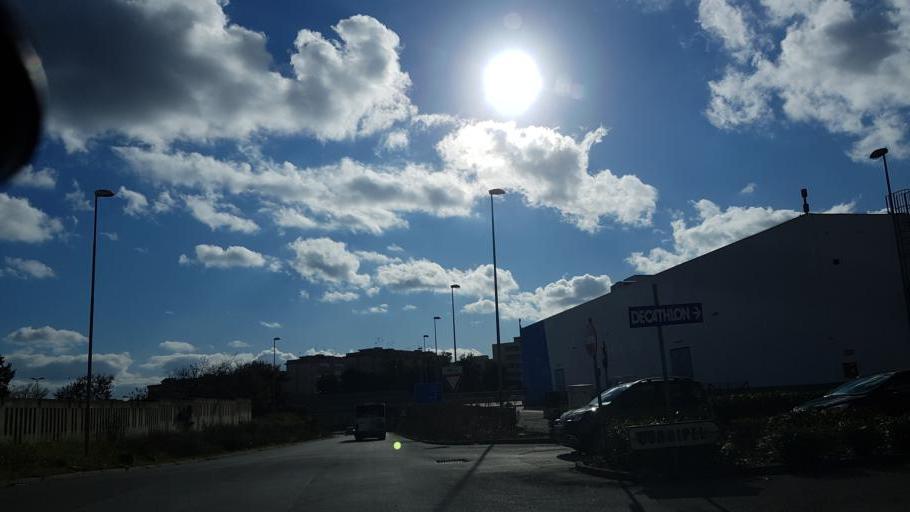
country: IT
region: Apulia
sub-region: Provincia di Brindisi
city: Brindisi
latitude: 40.6234
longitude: 17.9108
